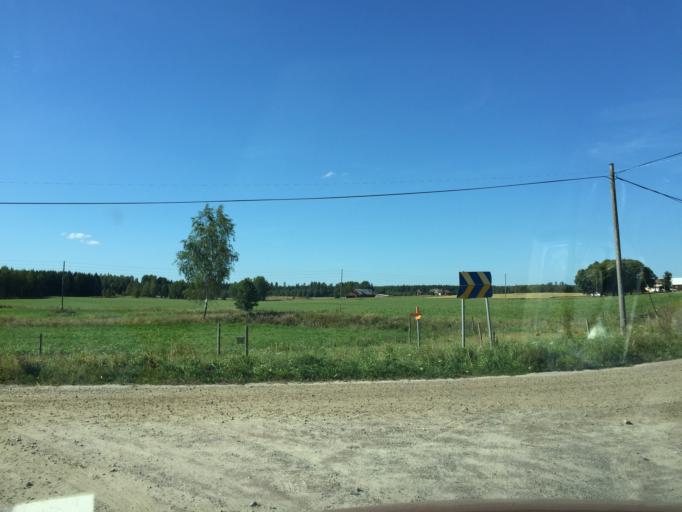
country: SE
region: OEstergoetland
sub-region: Finspangs Kommun
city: Finspang
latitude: 58.8919
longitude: 15.6686
